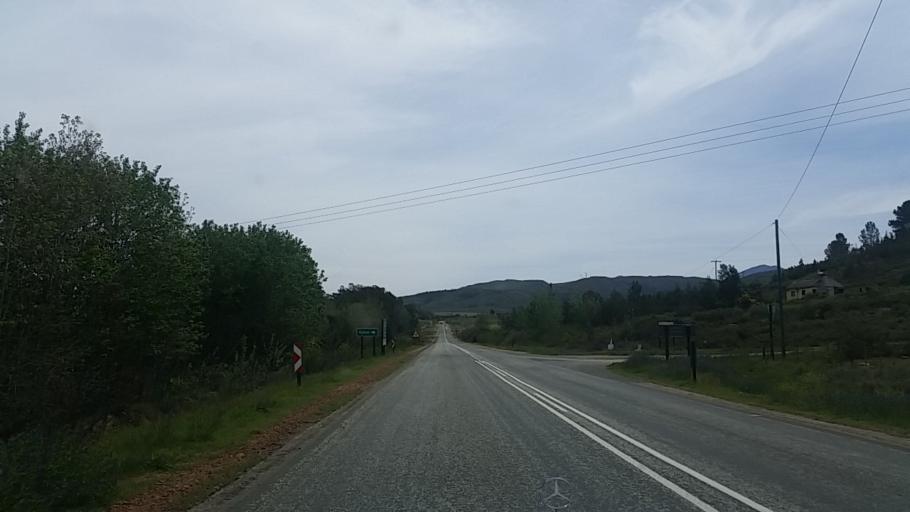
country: ZA
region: Western Cape
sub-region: Eden District Municipality
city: Knysna
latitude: -33.7722
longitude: 22.8998
